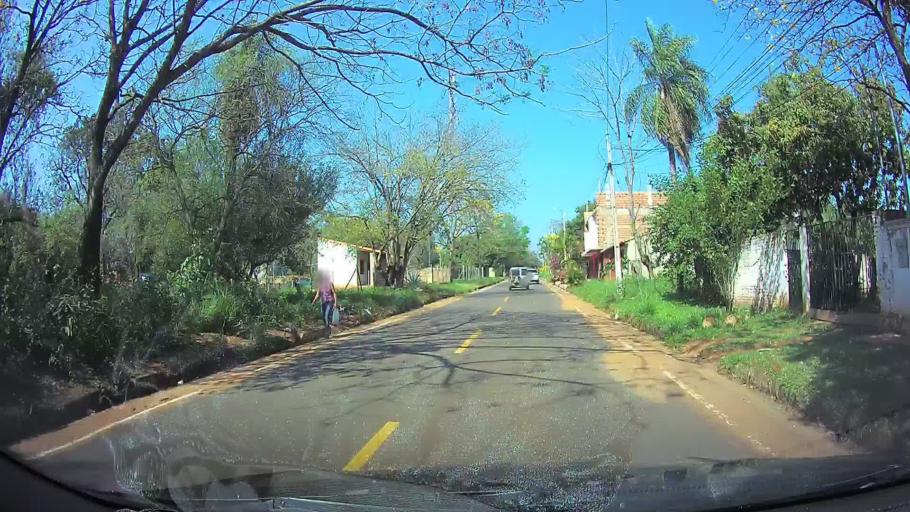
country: PY
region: Central
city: Limpio
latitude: -25.2364
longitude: -57.4846
